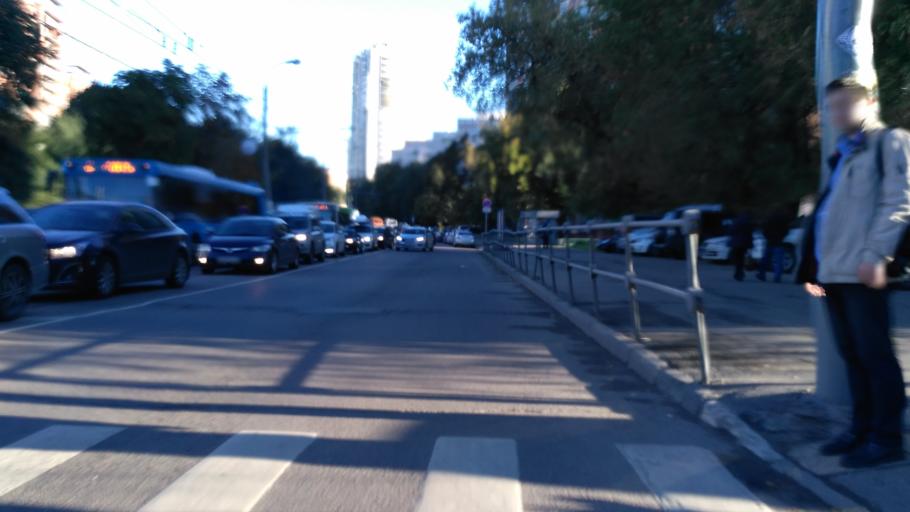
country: RU
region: Moscow
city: Likhobory
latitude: 55.8577
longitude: 37.5624
